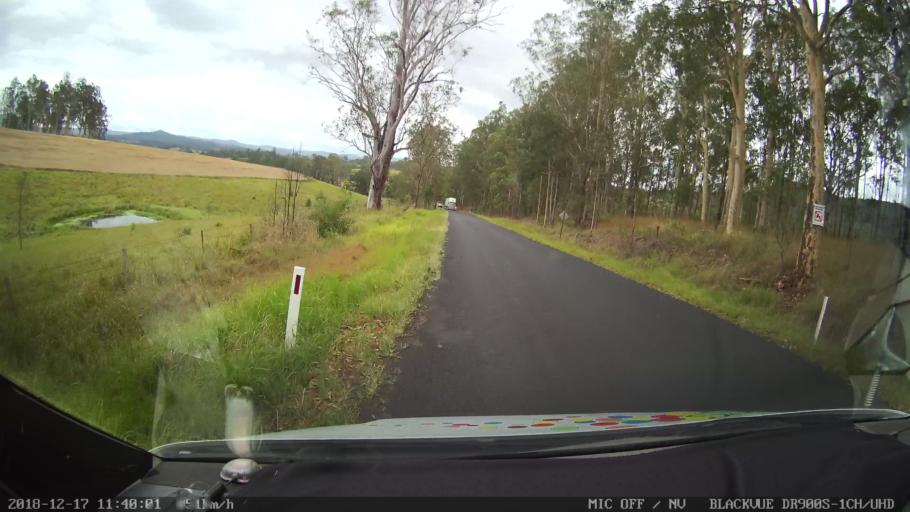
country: AU
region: New South Wales
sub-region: Kyogle
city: Kyogle
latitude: -28.6858
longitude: 152.5926
